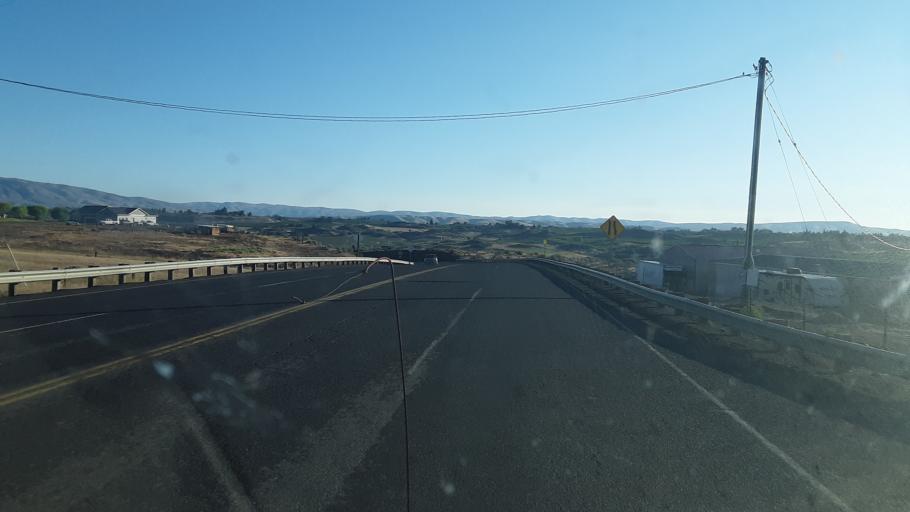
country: US
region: Washington
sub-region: Yakima County
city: Gleed
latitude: 46.6269
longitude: -120.6705
